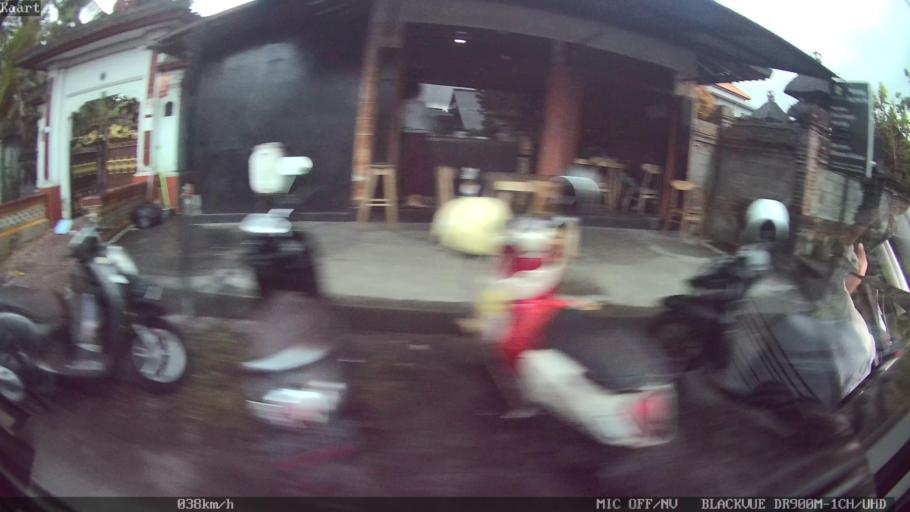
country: ID
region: Bali
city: Banjar Batur
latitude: -8.5988
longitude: 115.2058
